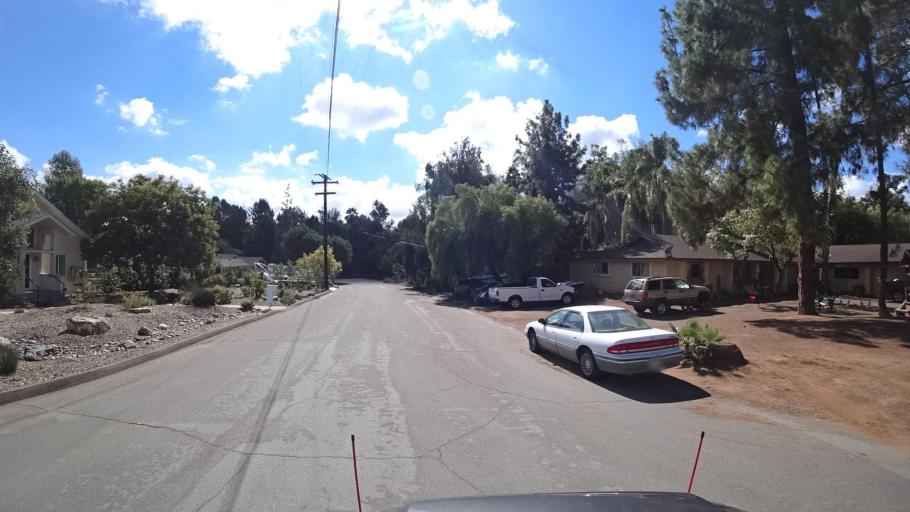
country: US
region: California
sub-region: San Diego County
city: Rancho San Diego
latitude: 32.7600
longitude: -116.9467
